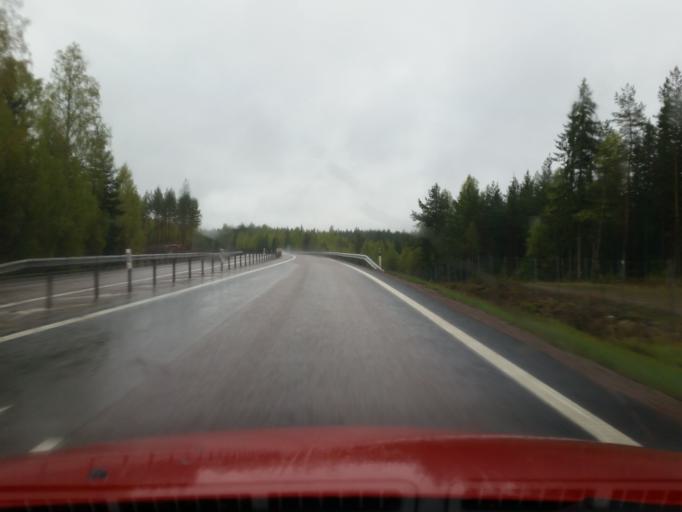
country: SE
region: Dalarna
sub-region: Saters Kommun
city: Saeter
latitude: 60.3605
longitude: 15.7229
